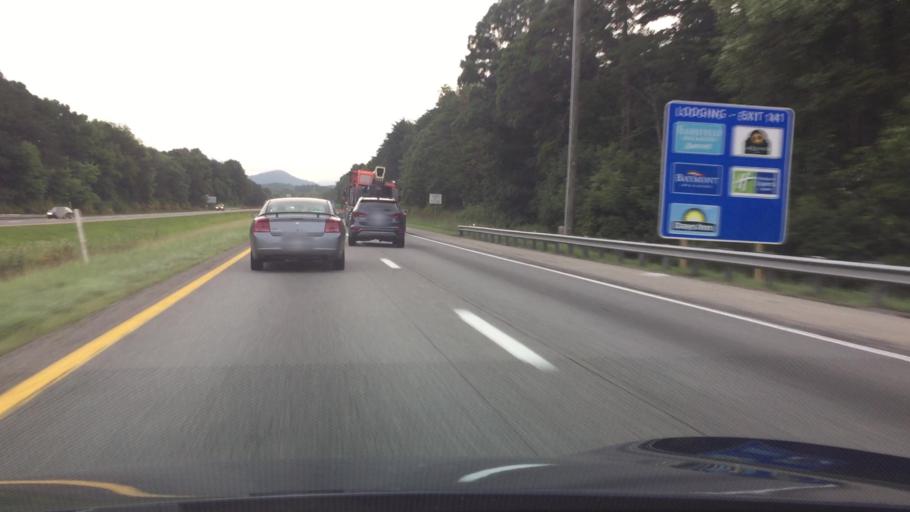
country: US
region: Virginia
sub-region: City of Salem
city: Salem
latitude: 37.3375
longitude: -80.0104
